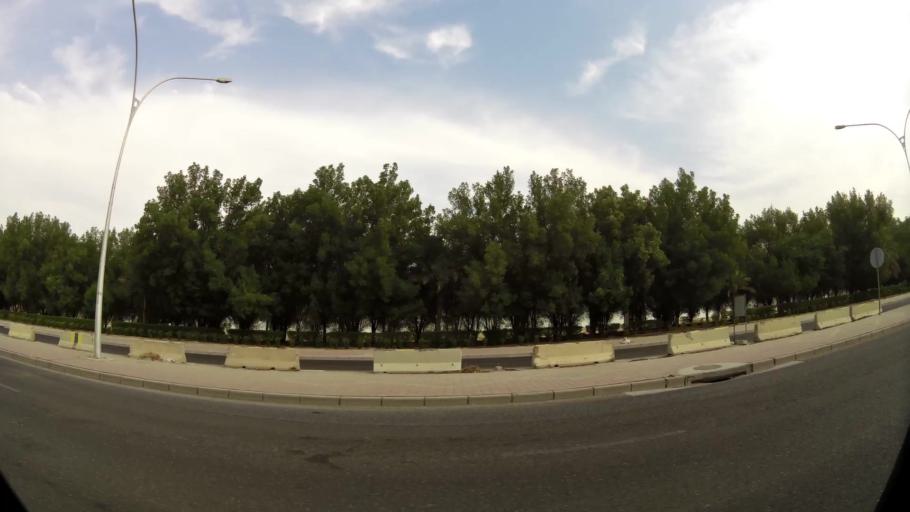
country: KW
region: Al Asimah
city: Ar Rabiyah
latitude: 29.3188
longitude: 47.8436
